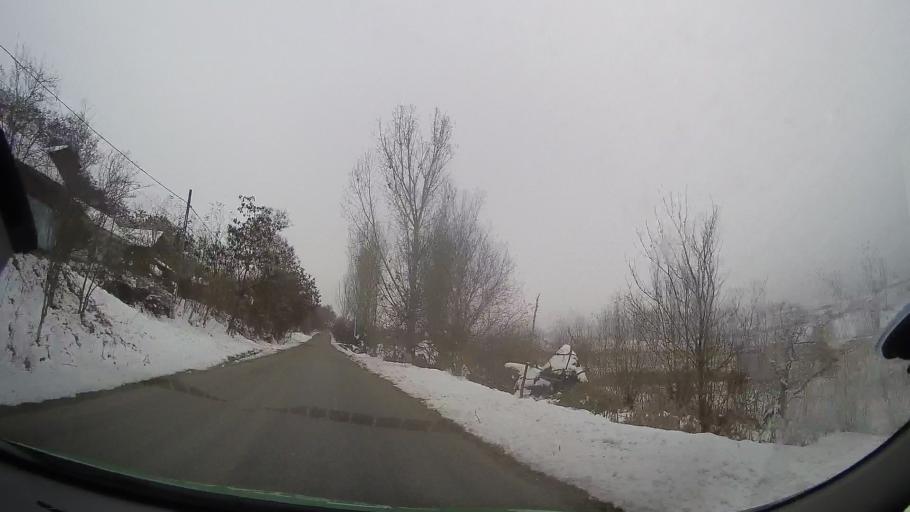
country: RO
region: Bacau
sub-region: Comuna Vultureni
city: Vultureni
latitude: 46.3568
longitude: 27.2894
